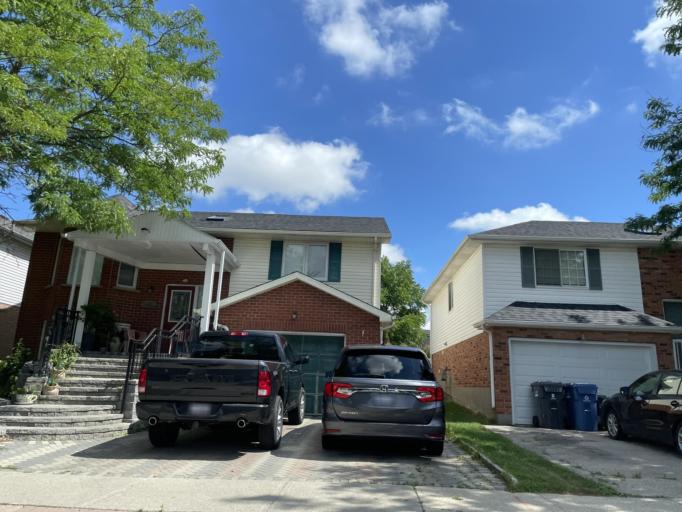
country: CA
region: Ontario
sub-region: Wellington County
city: Guelph
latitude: 43.5159
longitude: -80.2155
